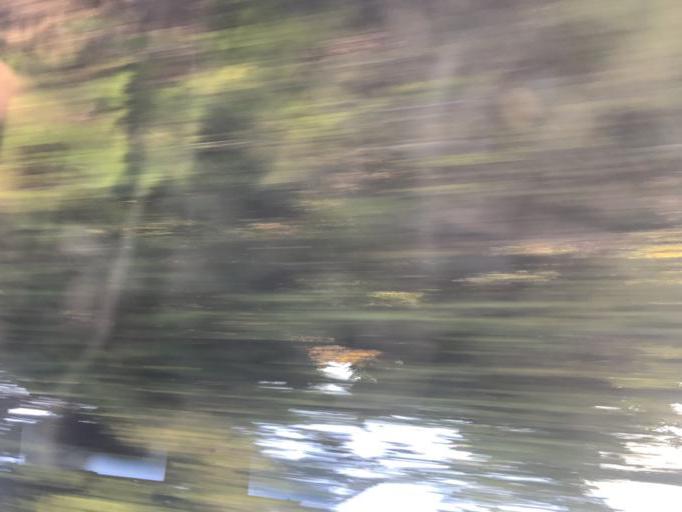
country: DK
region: Zealand
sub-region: Stevns Kommune
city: Store Heddinge
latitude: 55.3269
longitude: 12.3594
